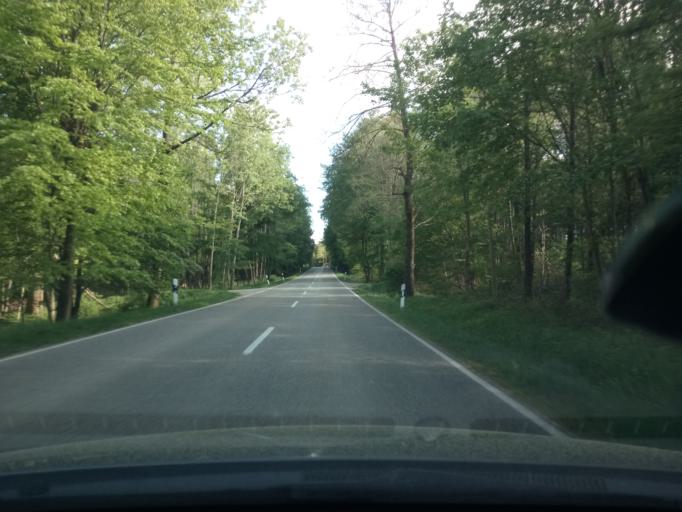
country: DE
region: Bavaria
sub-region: Upper Bavaria
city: Reichertsheim
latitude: 48.2106
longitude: 12.3017
